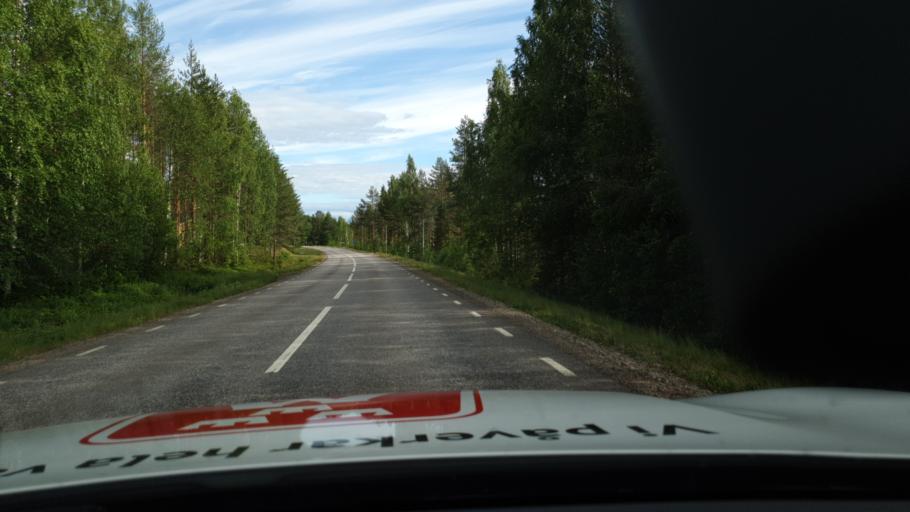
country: SE
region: Norrbotten
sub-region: Overkalix Kommun
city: OEverkalix
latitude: 66.4907
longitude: 22.7769
